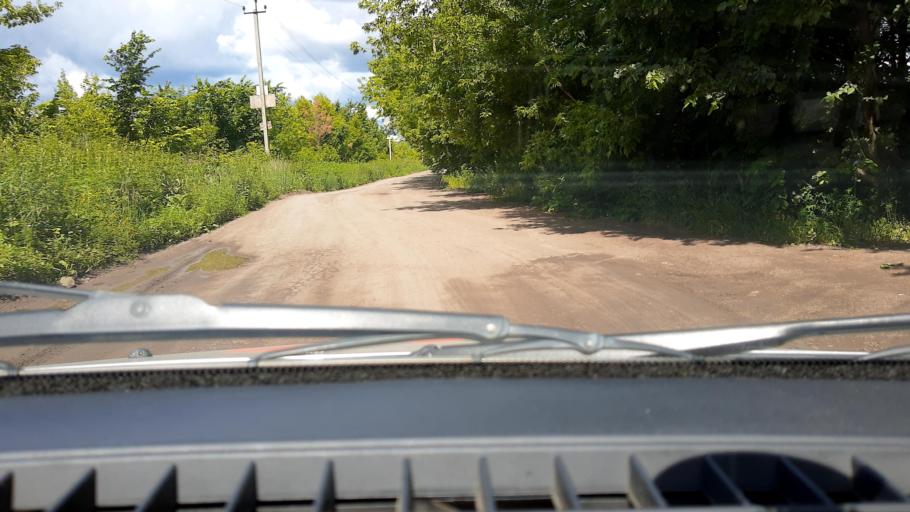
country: RU
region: Bashkortostan
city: Ufa
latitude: 54.6913
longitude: 56.0525
